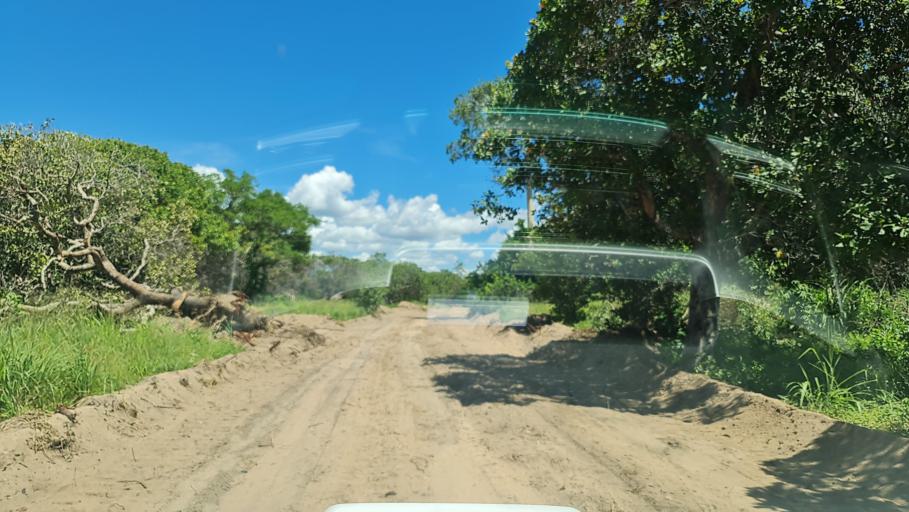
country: MZ
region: Nampula
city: Nampula
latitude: -15.3020
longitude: 39.8734
